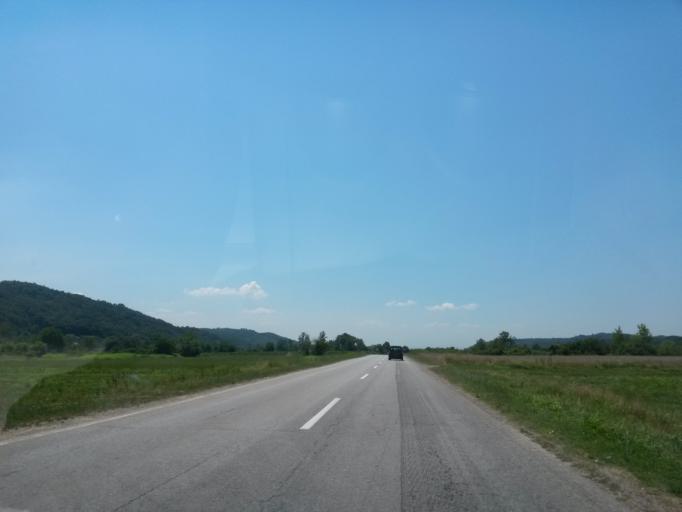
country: BA
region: Federation of Bosnia and Herzegovina
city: Lukavica
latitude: 44.9143
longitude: 18.1064
